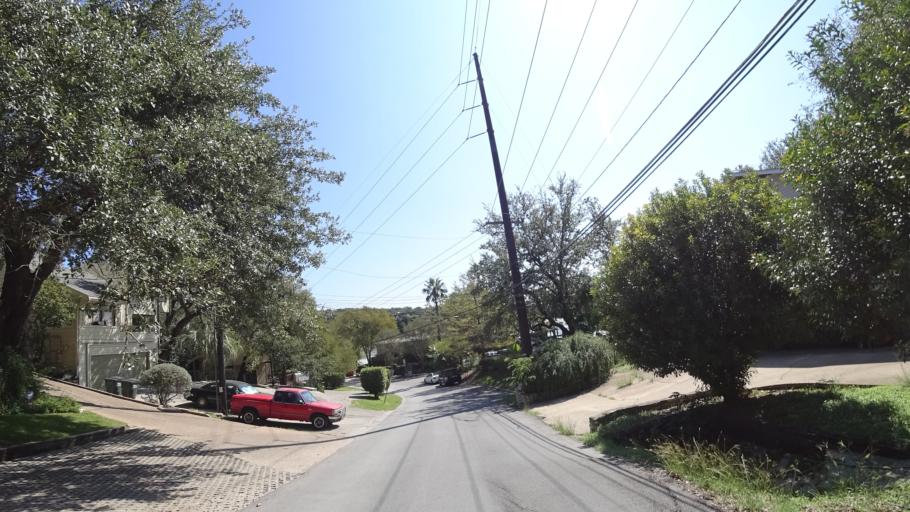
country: US
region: Texas
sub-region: Travis County
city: West Lake Hills
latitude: 30.3030
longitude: -97.7856
